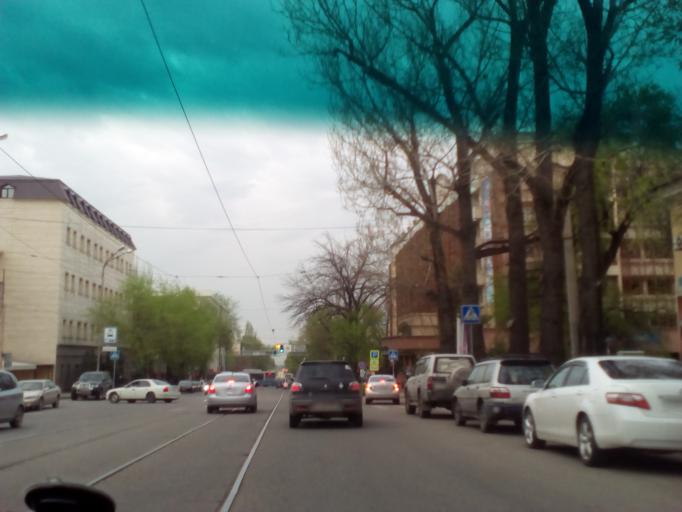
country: KZ
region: Almaty Qalasy
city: Almaty
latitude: 43.2625
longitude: 76.9492
